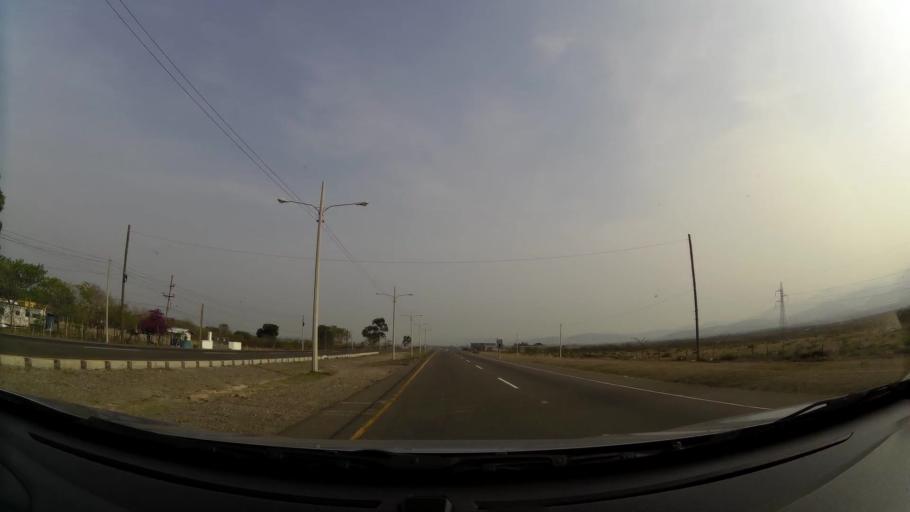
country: HN
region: Comayagua
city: Comayagua
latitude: 14.4024
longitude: -87.6189
